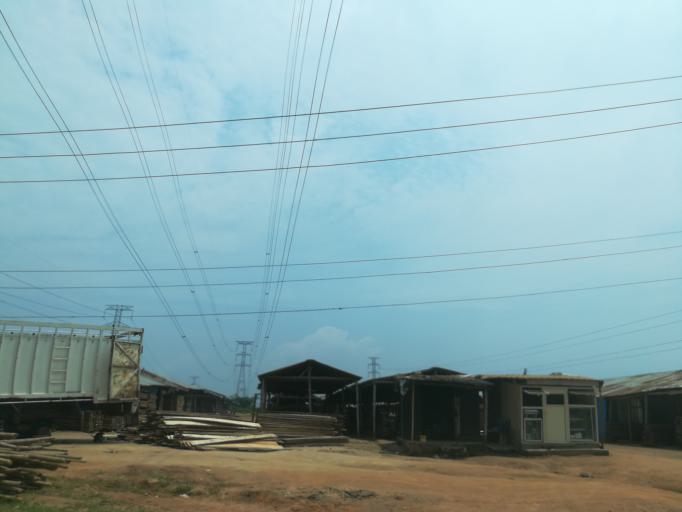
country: NG
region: Lagos
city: Ikorodu
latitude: 6.6074
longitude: 3.5894
